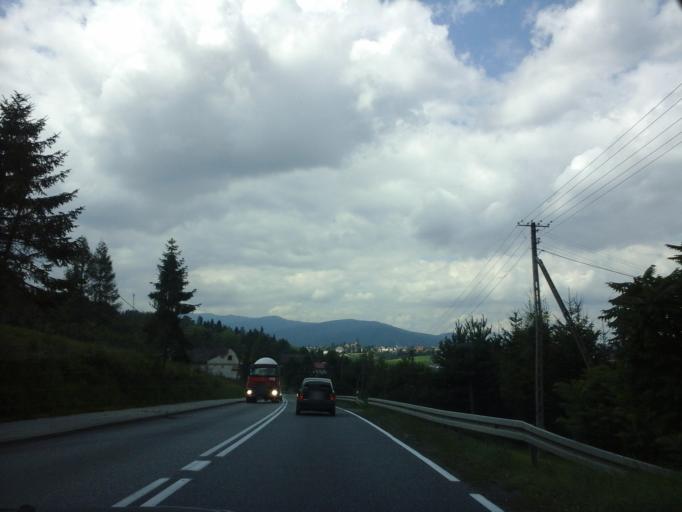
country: PL
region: Lesser Poland Voivodeship
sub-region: Powiat suski
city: Naprawa
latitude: 49.6455
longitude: 19.8568
